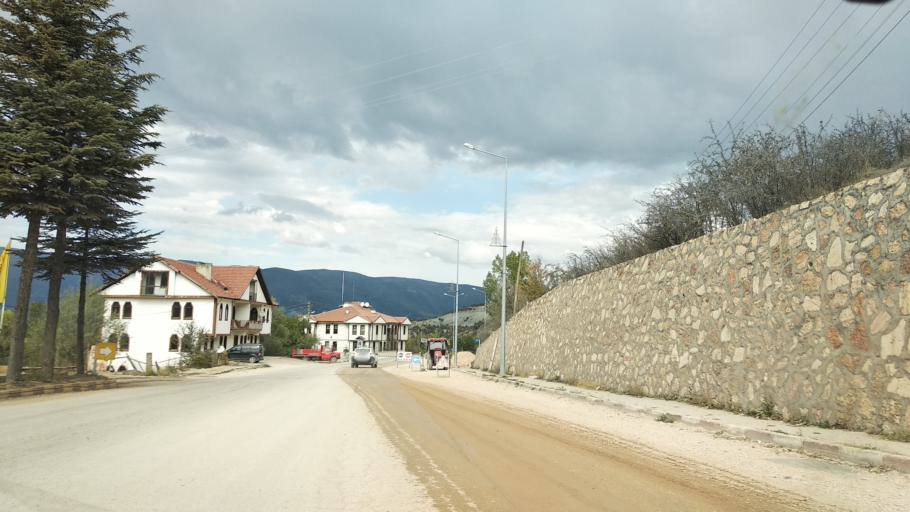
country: TR
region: Bolu
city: Mudurnu
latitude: 40.4734
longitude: 31.2095
